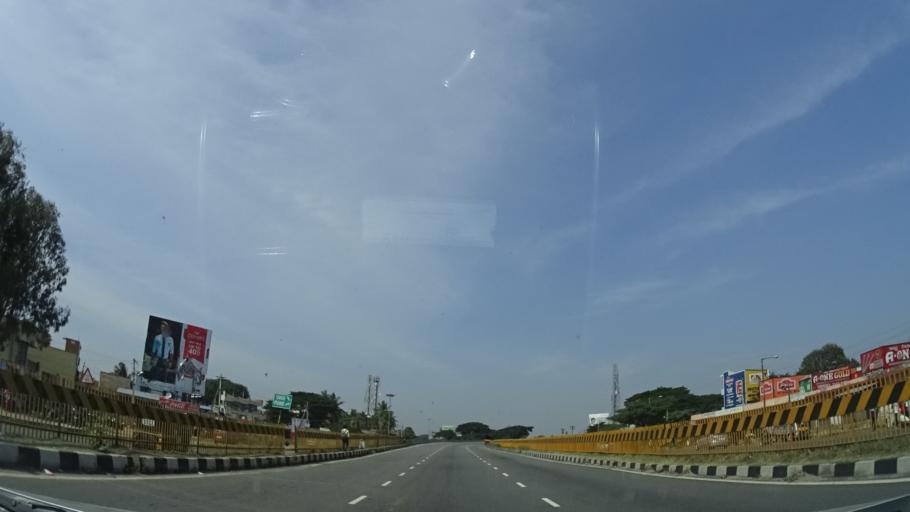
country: IN
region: Karnataka
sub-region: Tumkur
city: Tumkur
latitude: 13.3268
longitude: 77.1328
